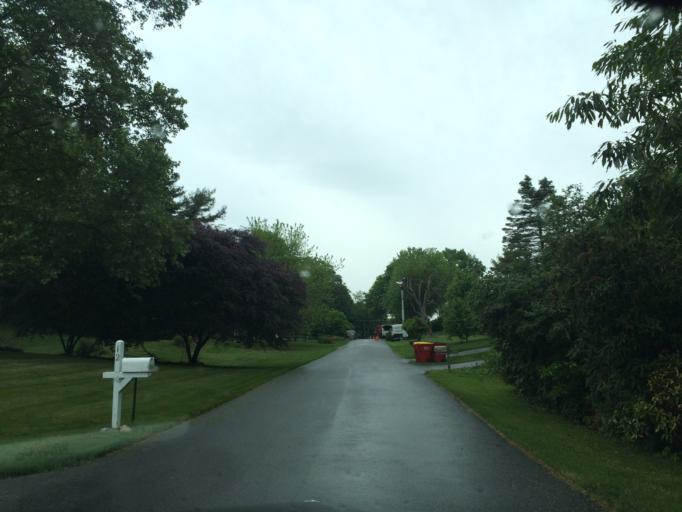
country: US
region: Maryland
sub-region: Washington County
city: Robinwood
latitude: 39.6169
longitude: -77.6824
